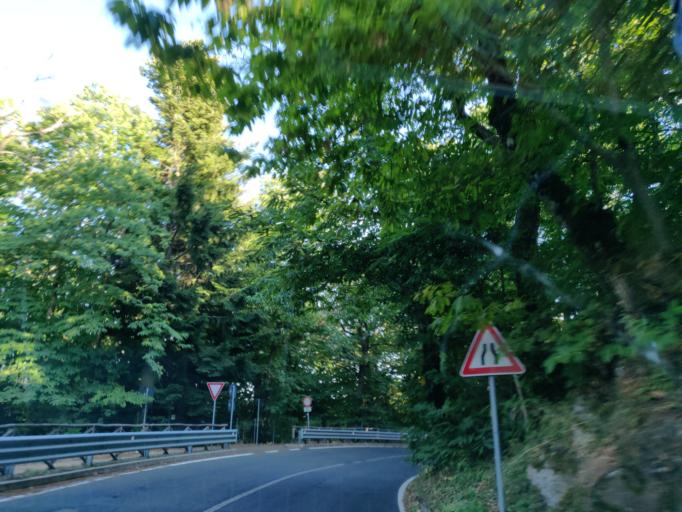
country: IT
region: Tuscany
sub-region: Provincia di Siena
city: Piancastagnaio
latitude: 42.8573
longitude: 11.6840
